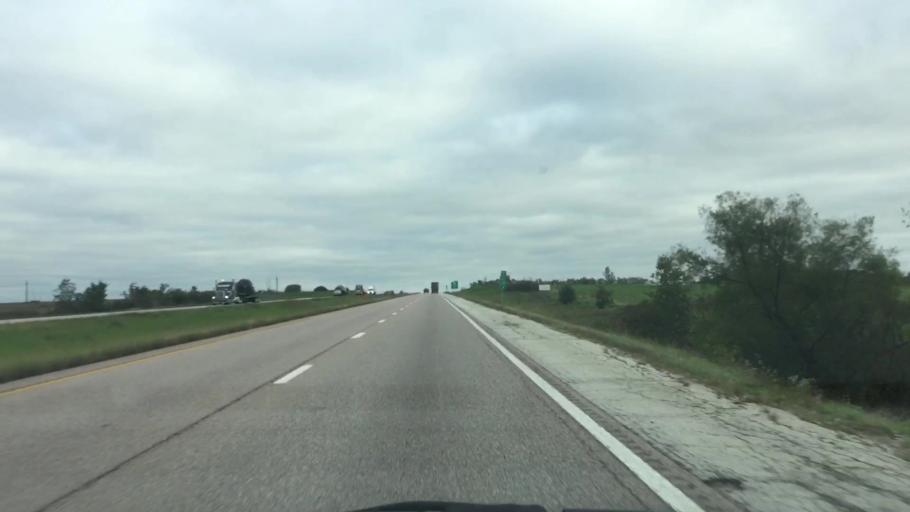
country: US
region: Missouri
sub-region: Clinton County
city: Lathrop
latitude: 39.5291
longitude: -94.2788
